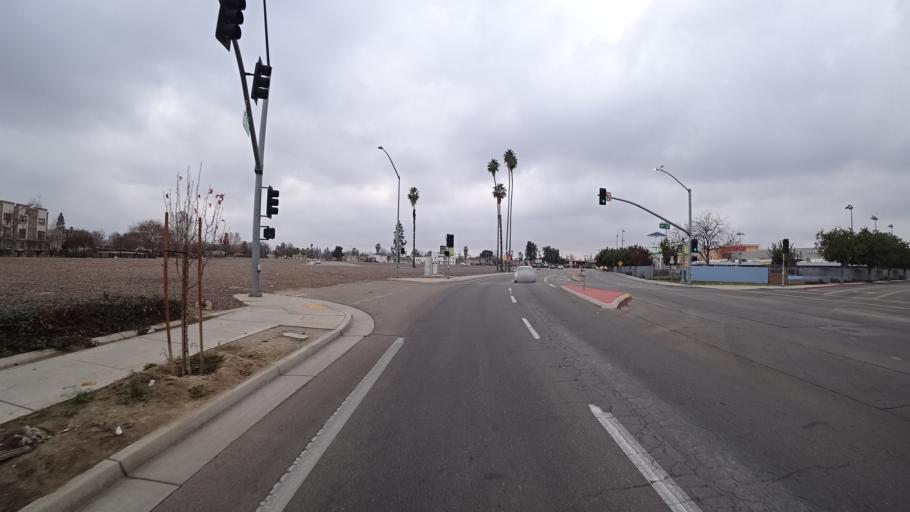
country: US
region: California
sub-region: Kern County
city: Bakersfield
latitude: 35.3704
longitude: -119.0106
